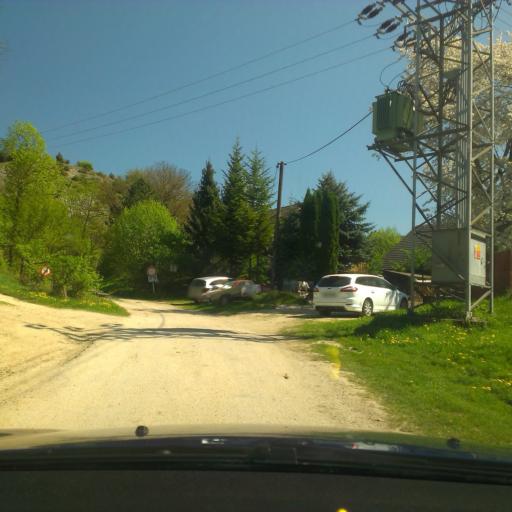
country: SK
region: Trnavsky
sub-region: Okres Trnava
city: Piestany
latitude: 48.6612
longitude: 17.8918
